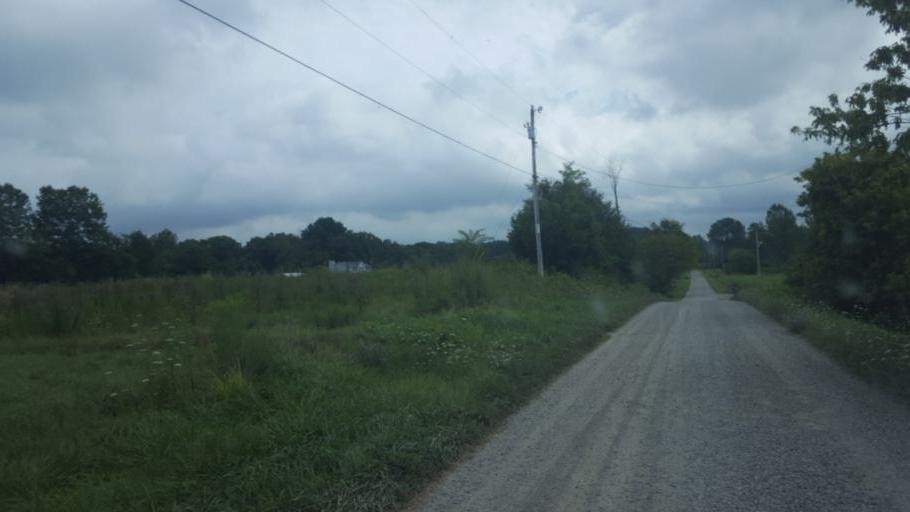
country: US
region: Ohio
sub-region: Morrow County
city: Mount Gilead
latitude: 40.5012
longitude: -82.7410
